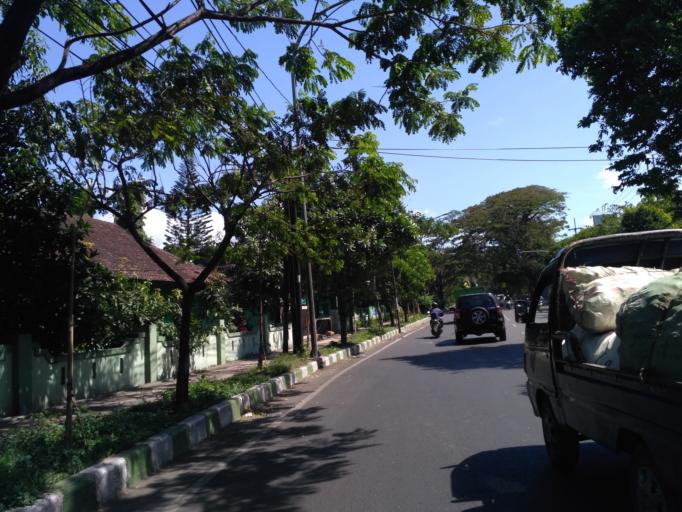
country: ID
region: East Java
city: Malang
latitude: -7.9786
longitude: 112.6458
